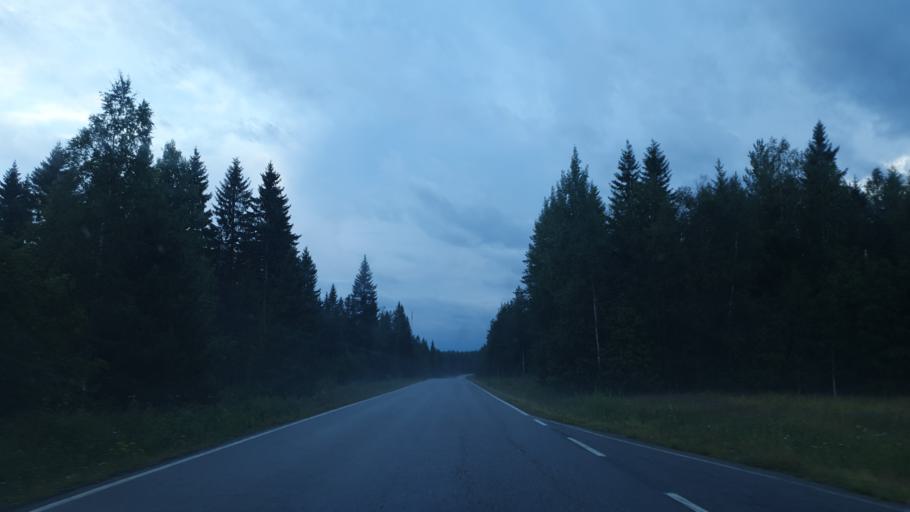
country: FI
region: Kainuu
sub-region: Kehys-Kainuu
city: Kuhmo
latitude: 63.9563
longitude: 29.7107
